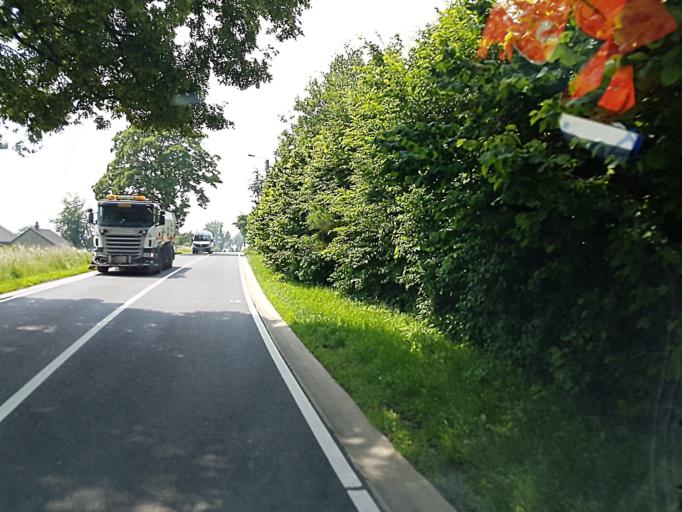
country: BE
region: Wallonia
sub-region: Province de Liege
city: Lierneux
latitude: 50.3334
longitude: 5.7831
